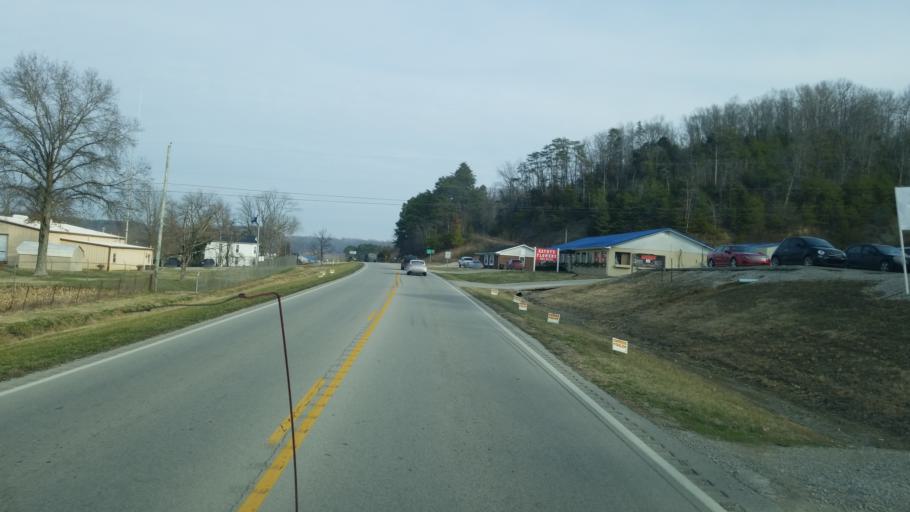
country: US
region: Kentucky
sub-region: Casey County
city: Liberty
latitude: 37.3029
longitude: -84.9463
